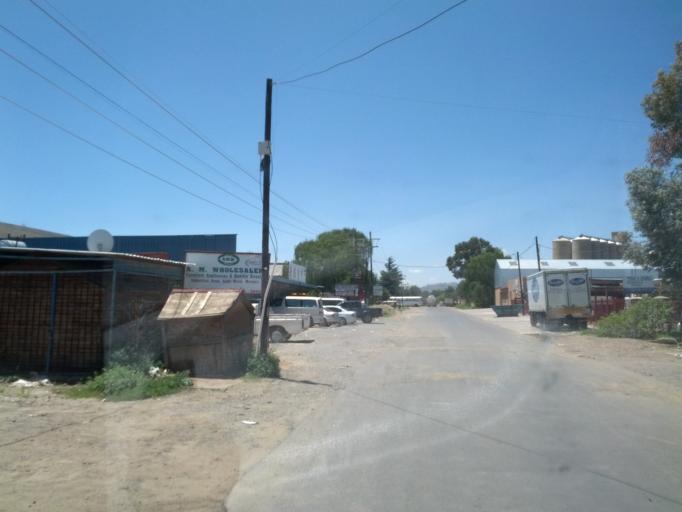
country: LS
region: Maseru
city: Maseru
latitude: -29.2959
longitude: 27.4755
